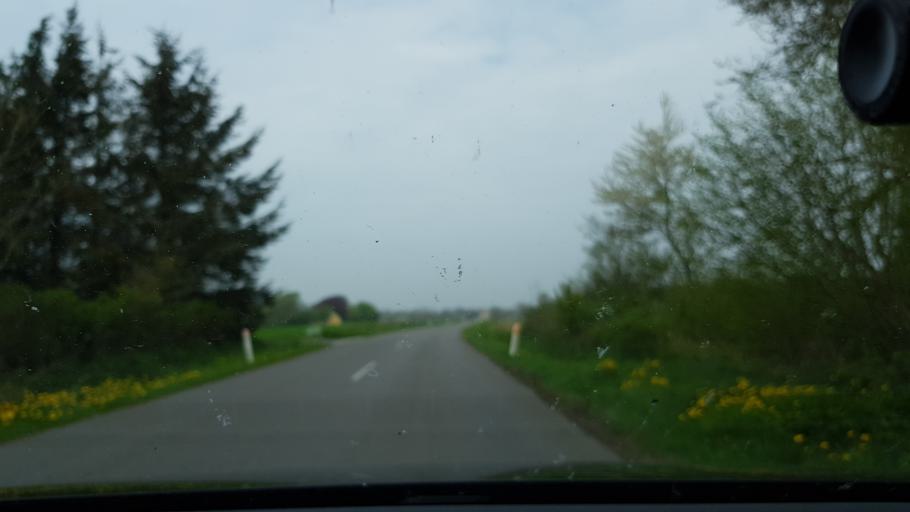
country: DK
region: Capital Region
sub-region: Bornholm Kommune
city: Nexo
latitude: 55.0197
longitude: 15.0966
